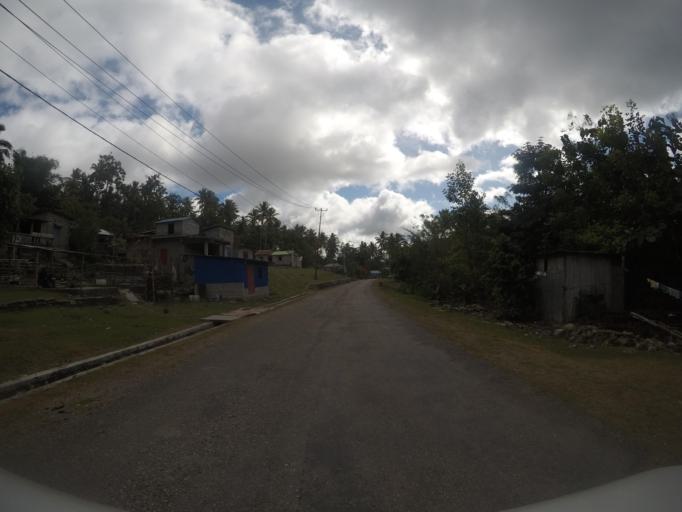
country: TL
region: Lautem
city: Lospalos
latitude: -8.5341
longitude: 126.9178
